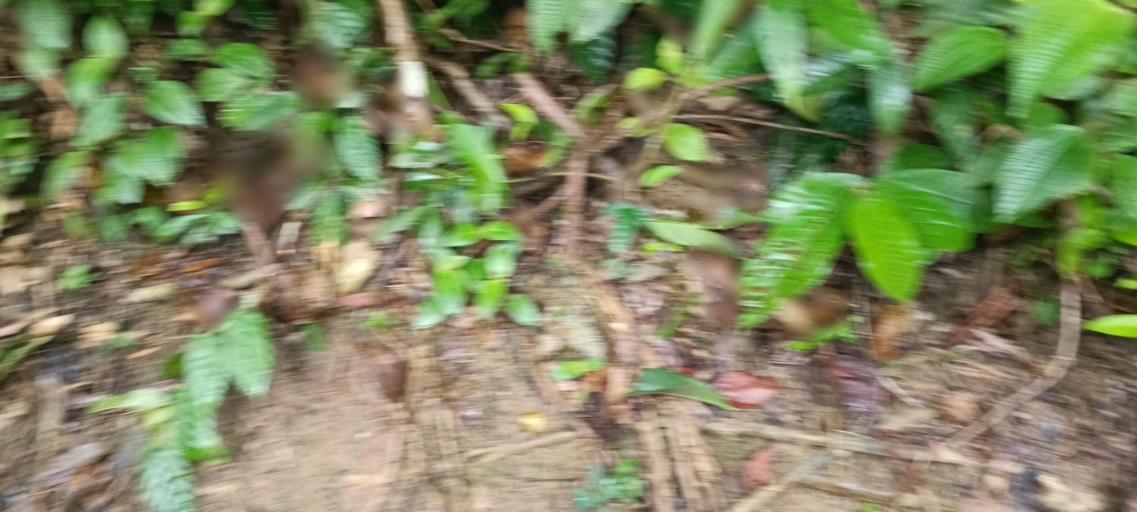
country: MY
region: Penang
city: Bukit Mertajam
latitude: 5.3663
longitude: 100.4751
